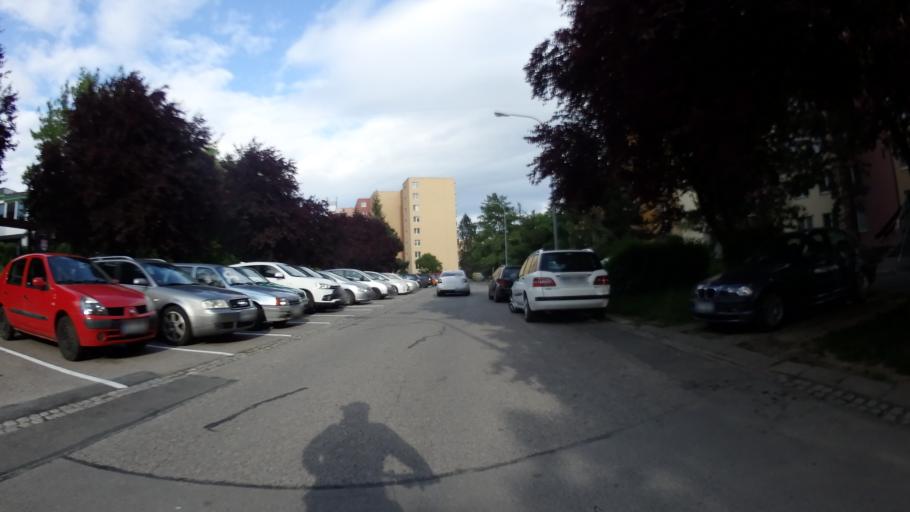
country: CZ
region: South Moravian
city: Moravany
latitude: 49.1695
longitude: 16.5809
